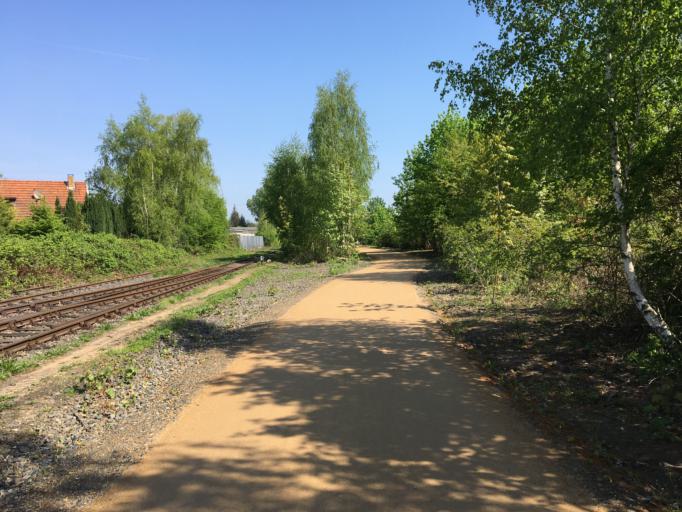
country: DE
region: Lower Saxony
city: Braunschweig
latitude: 52.2798
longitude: 10.5347
